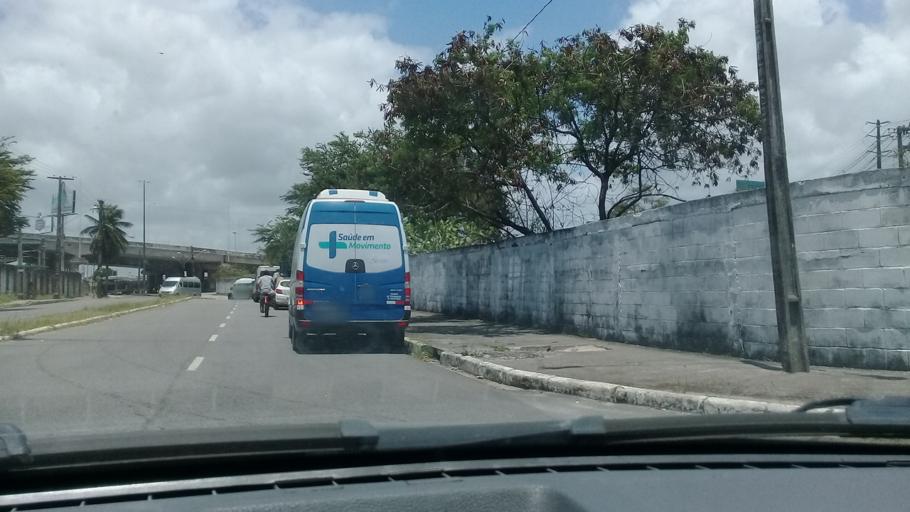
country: BR
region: Pernambuco
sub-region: Recife
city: Recife
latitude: -8.0725
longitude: -34.8924
